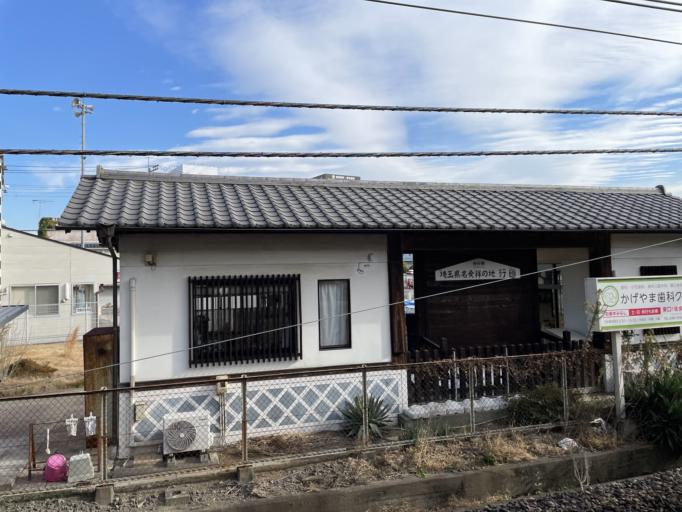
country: JP
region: Saitama
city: Fukiage-fujimi
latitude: 36.1142
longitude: 139.4320
